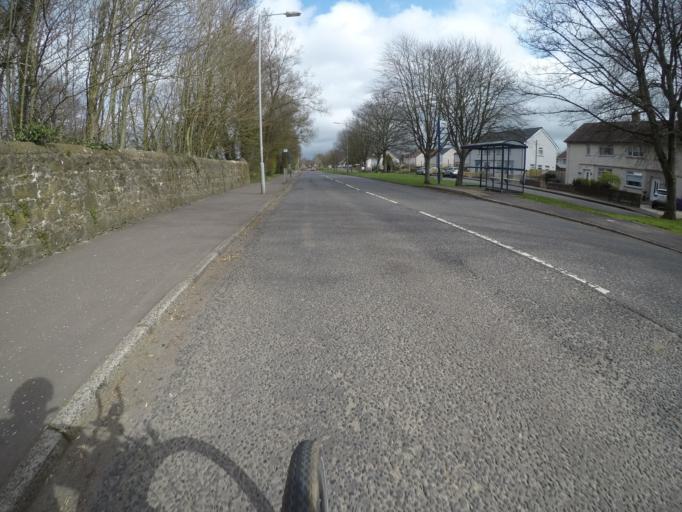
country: GB
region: Scotland
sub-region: North Ayrshire
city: Irvine
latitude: 55.6255
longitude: -4.6419
